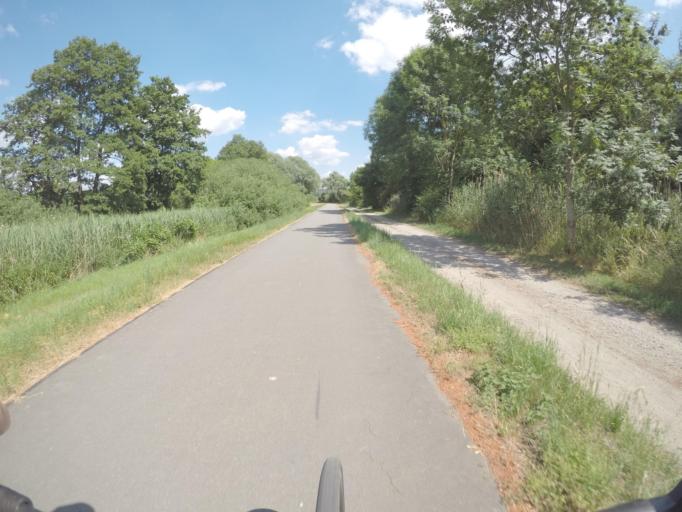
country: DE
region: Brandenburg
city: Roskow
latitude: 52.4367
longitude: 12.6931
